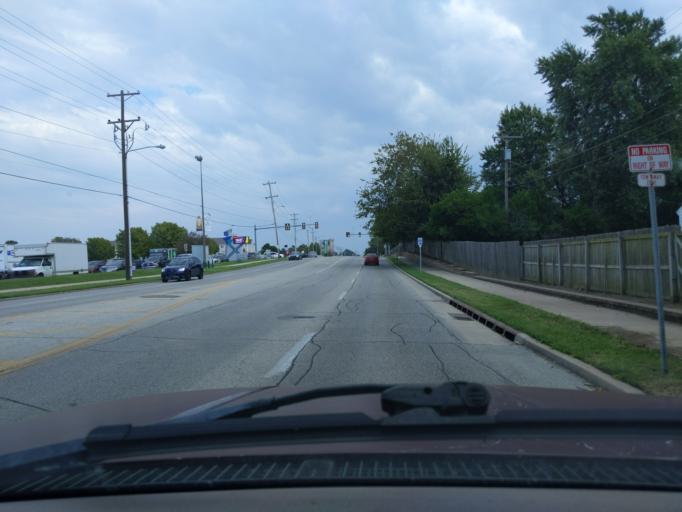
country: US
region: Oklahoma
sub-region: Tulsa County
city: Tulsa
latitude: 36.1332
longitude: -95.9289
